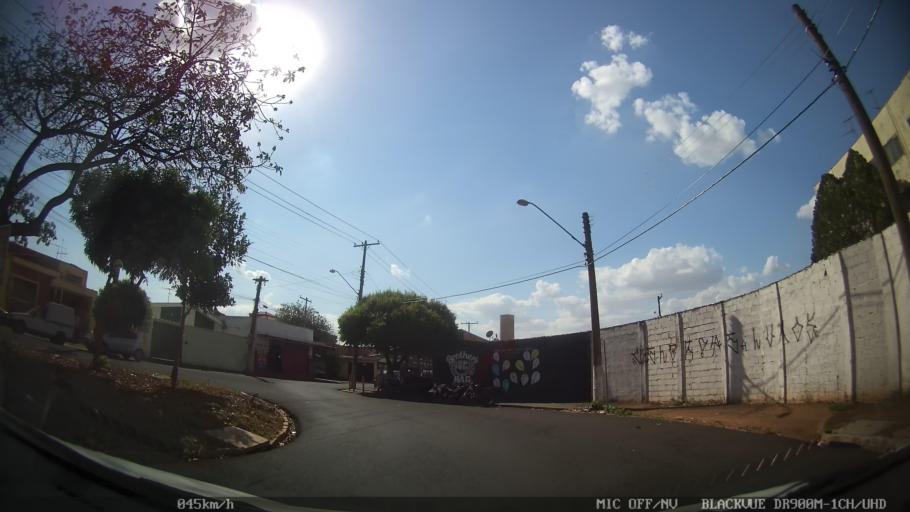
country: BR
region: Sao Paulo
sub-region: Ribeirao Preto
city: Ribeirao Preto
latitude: -21.1887
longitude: -47.8257
